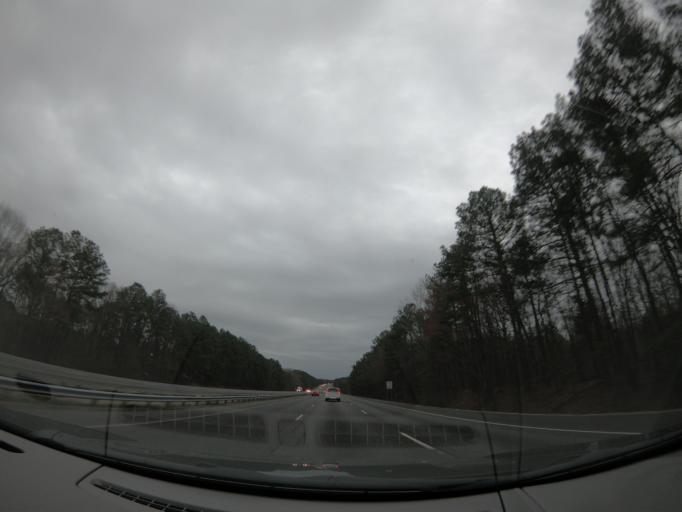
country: US
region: Georgia
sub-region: Gordon County
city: Calhoun
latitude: 34.6137
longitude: -84.9634
